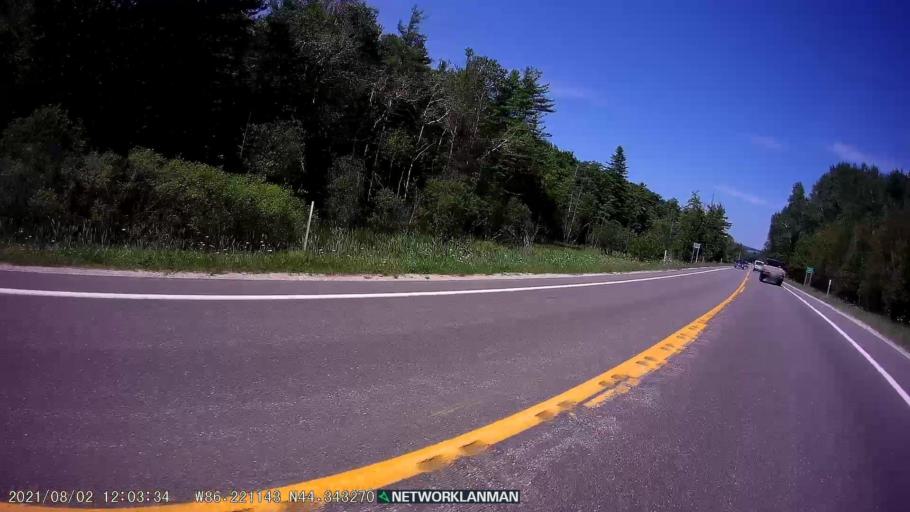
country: US
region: Michigan
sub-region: Manistee County
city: Manistee
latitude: 44.3435
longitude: -86.2211
